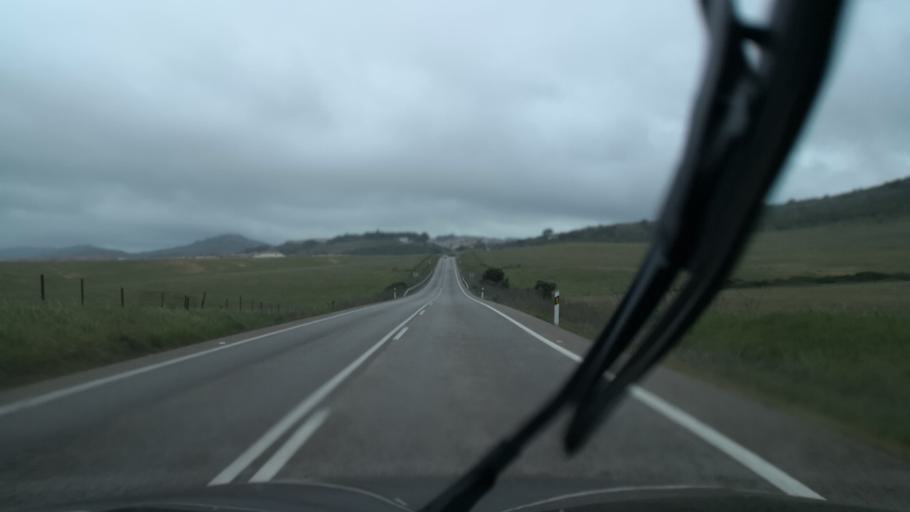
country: ES
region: Extremadura
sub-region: Provincia de Caceres
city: Caceres
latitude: 39.4984
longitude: -6.3875
